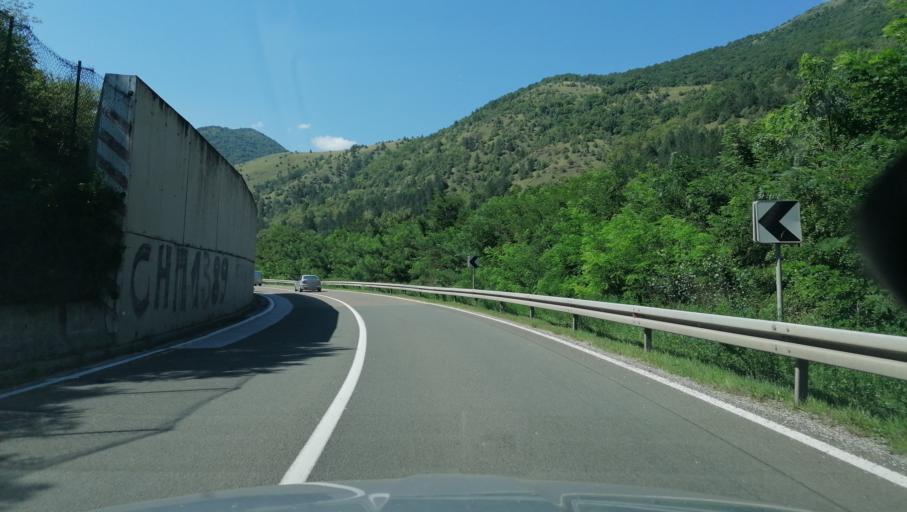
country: RS
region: Central Serbia
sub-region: Raski Okrug
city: Kraljevo
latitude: 43.5947
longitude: 20.5699
